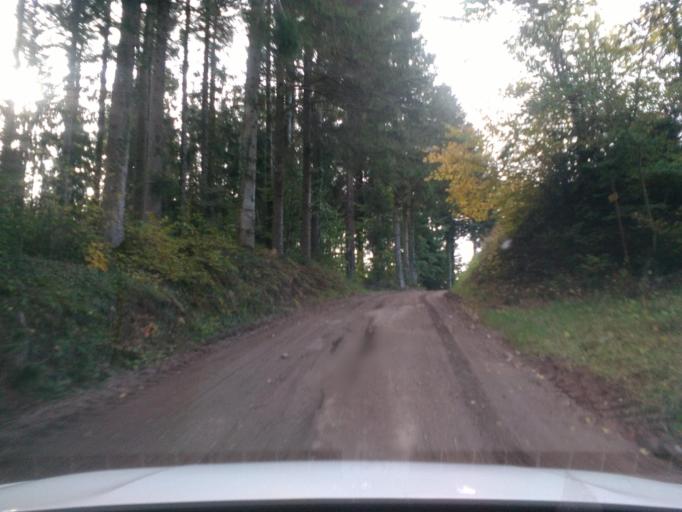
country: FR
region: Lorraine
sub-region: Departement des Vosges
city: Senones
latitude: 48.3902
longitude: 7.0026
